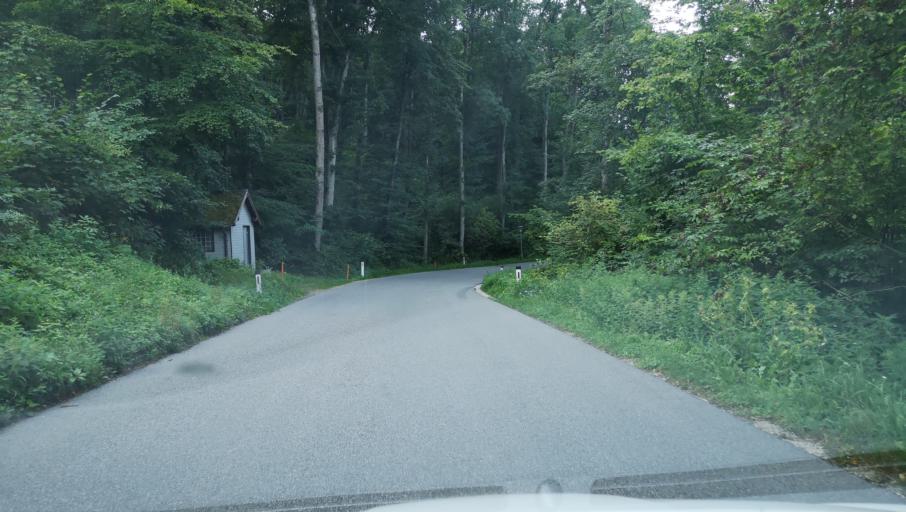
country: AT
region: Lower Austria
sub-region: Politischer Bezirk Amstetten
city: Sankt Georgen am Ybbsfelde
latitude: 48.1328
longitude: 14.9228
